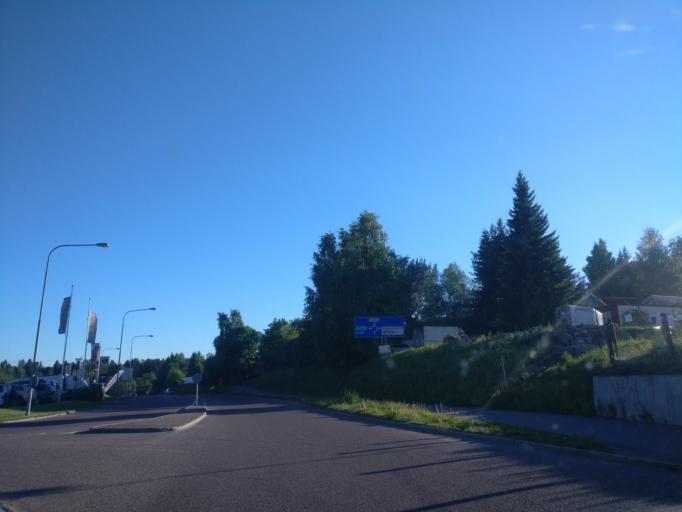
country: SE
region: Vaesternorrland
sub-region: Sundsvalls Kommun
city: Sundsvall
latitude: 62.4130
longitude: 17.3362
